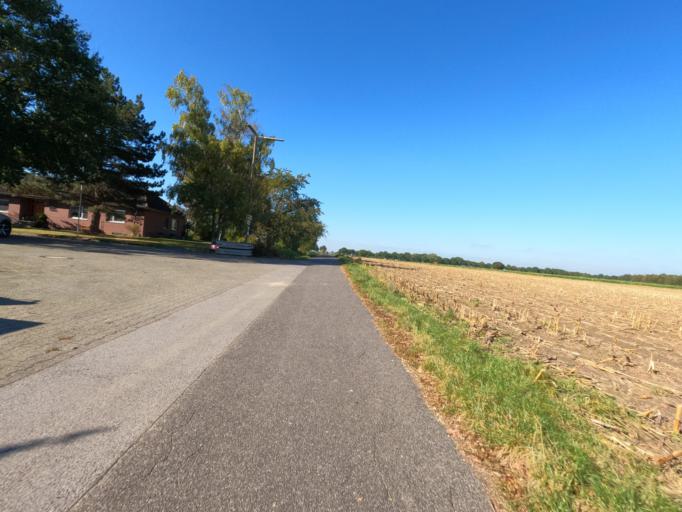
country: DE
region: North Rhine-Westphalia
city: Erkelenz
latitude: 51.0418
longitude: 6.2899
